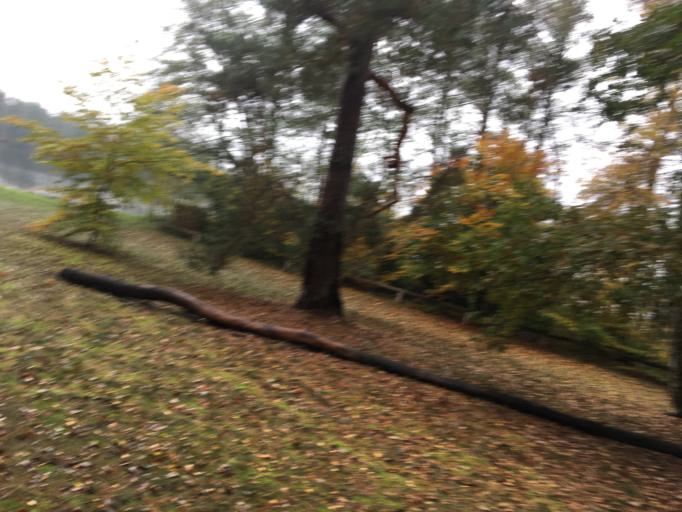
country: DE
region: Brandenburg
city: Briesen
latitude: 52.2640
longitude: 14.2940
